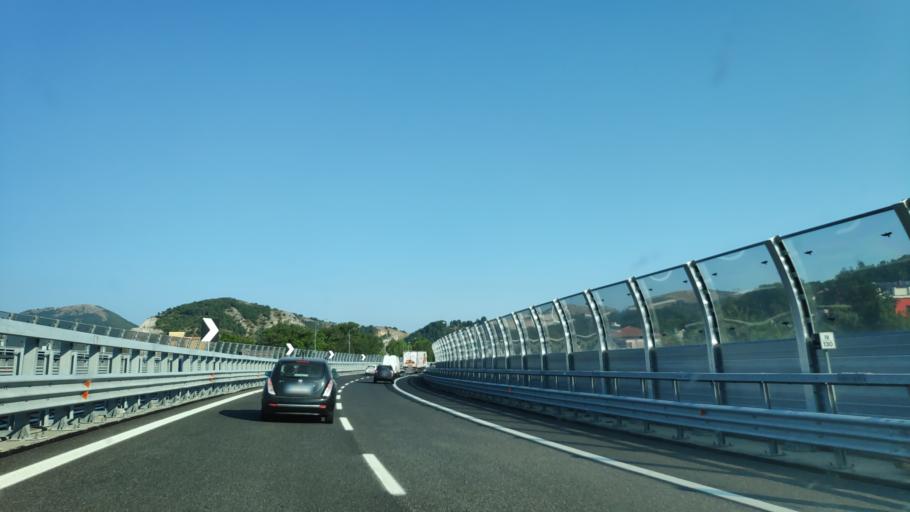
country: IT
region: Basilicate
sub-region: Provincia di Potenza
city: Lagonegro
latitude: 40.1315
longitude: 15.7627
